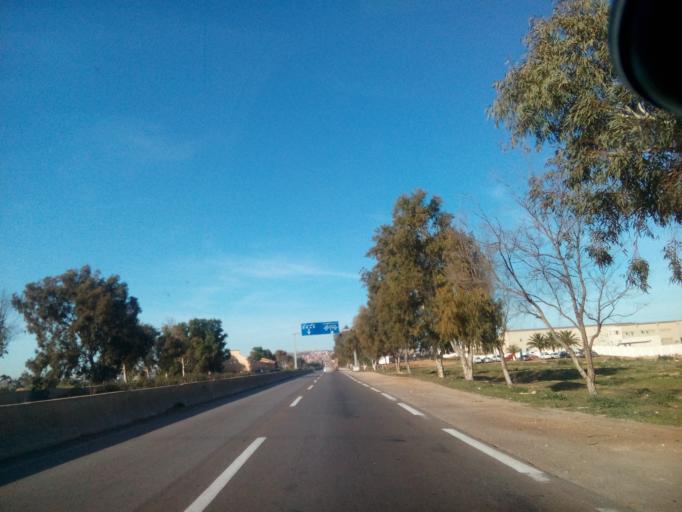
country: DZ
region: Oran
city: Ain el Bya
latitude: 35.7845
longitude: -0.1491
